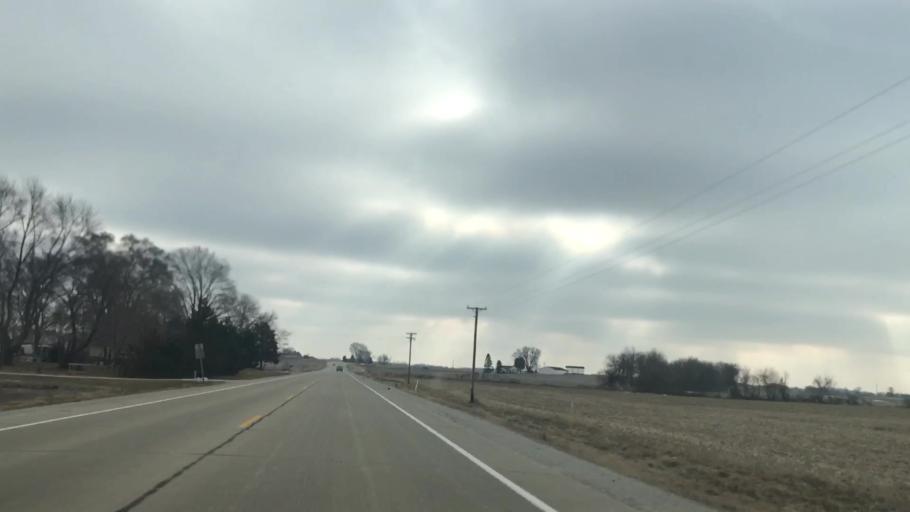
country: US
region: Wisconsin
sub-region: Dodge County
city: Beaver Dam
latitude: 43.4827
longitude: -88.7856
